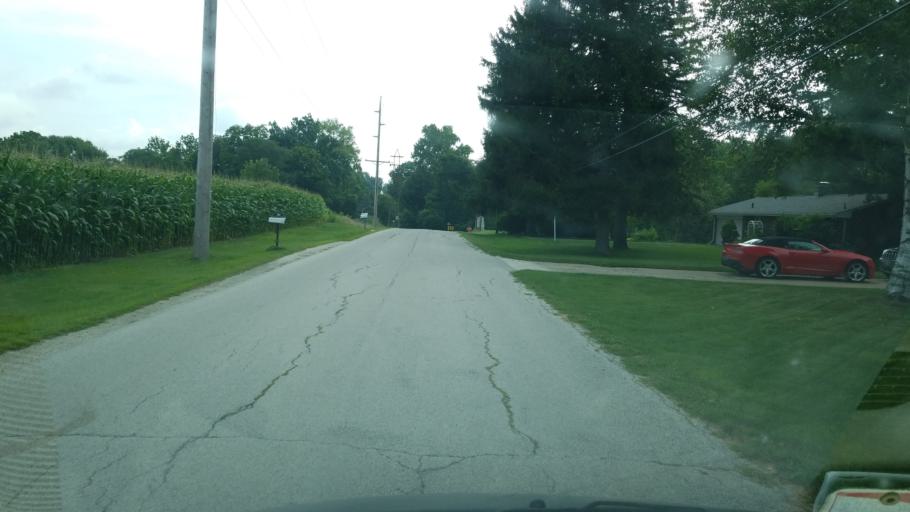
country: US
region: Ohio
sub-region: Sandusky County
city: Ballville
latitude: 41.2987
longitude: -83.1656
